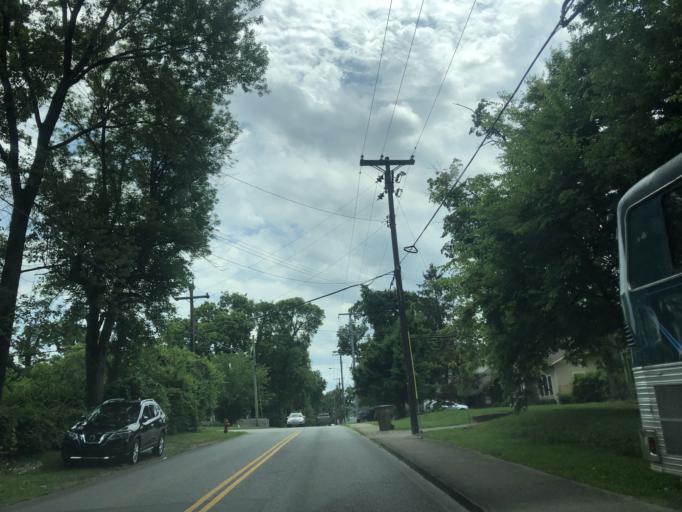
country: US
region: Tennessee
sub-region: Davidson County
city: Nashville
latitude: 36.1864
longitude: -86.7438
